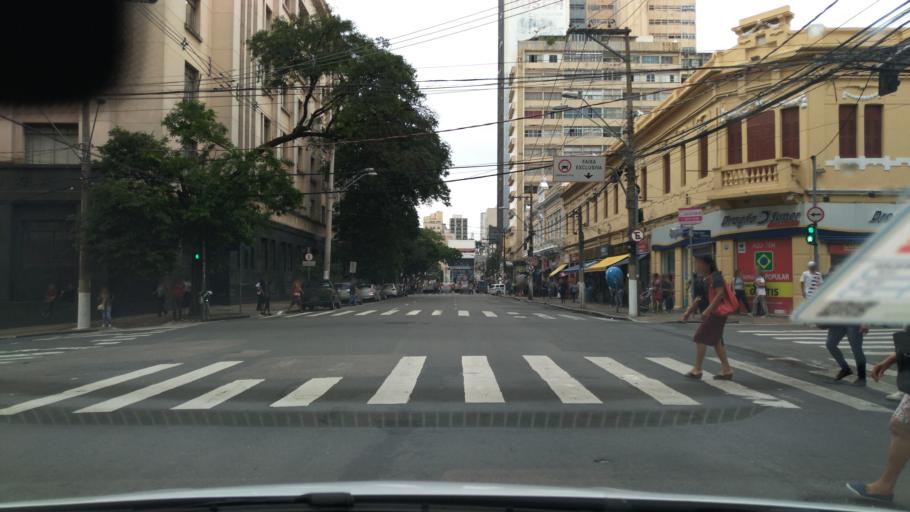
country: BR
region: Sao Paulo
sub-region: Campinas
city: Campinas
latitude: -22.9051
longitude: -47.0615
